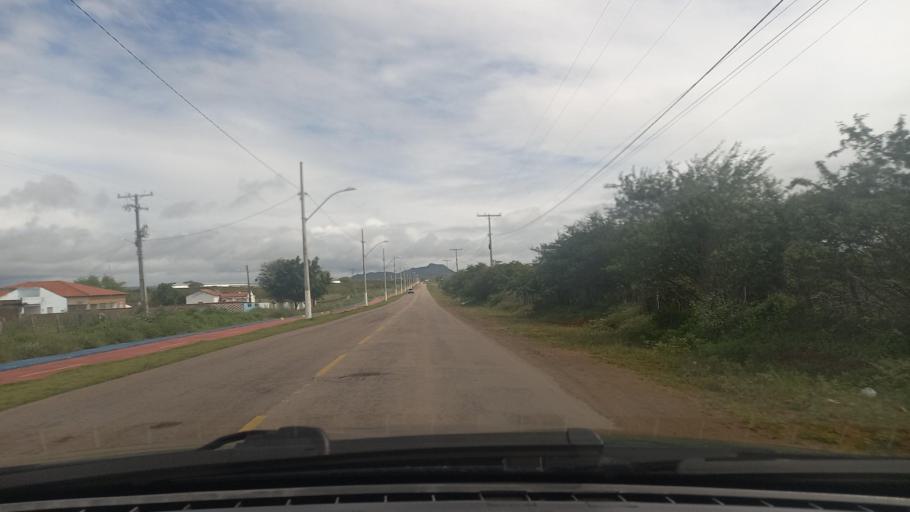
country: BR
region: Bahia
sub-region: Paulo Afonso
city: Paulo Afonso
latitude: -9.3530
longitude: -38.2651
